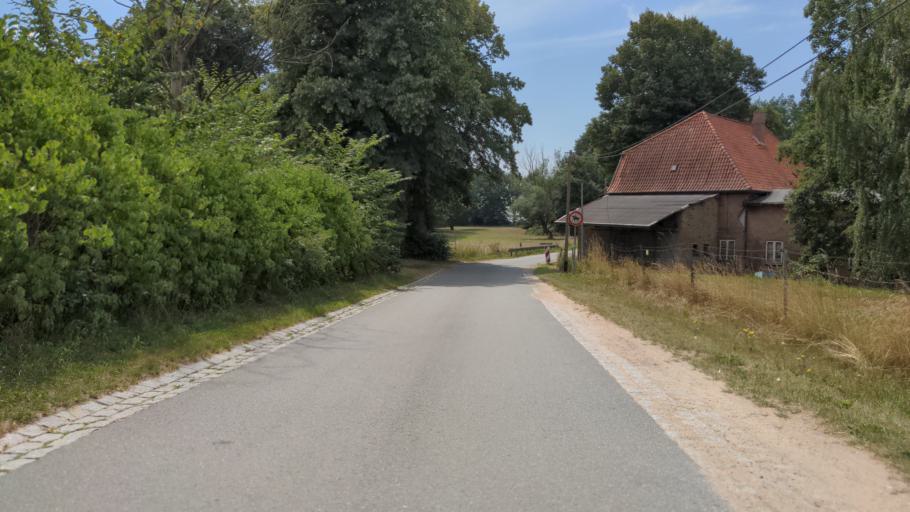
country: DE
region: Schleswig-Holstein
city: Gross Gronau
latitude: 53.8516
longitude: 10.7956
